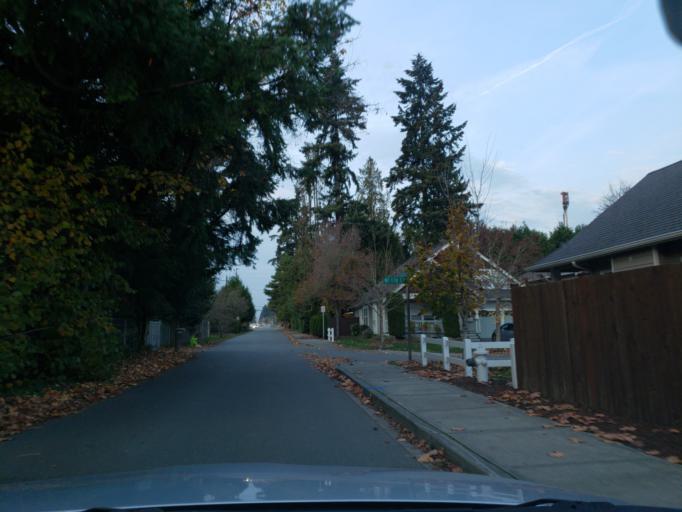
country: US
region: Washington
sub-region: King County
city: Bothell
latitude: 47.7571
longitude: -122.2235
